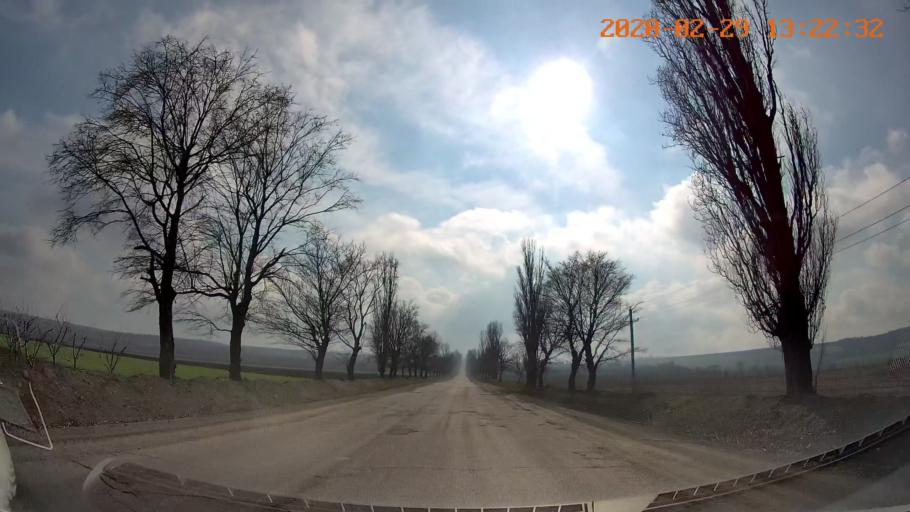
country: MD
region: Telenesti
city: Camenca
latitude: 47.9594
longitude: 28.6277
